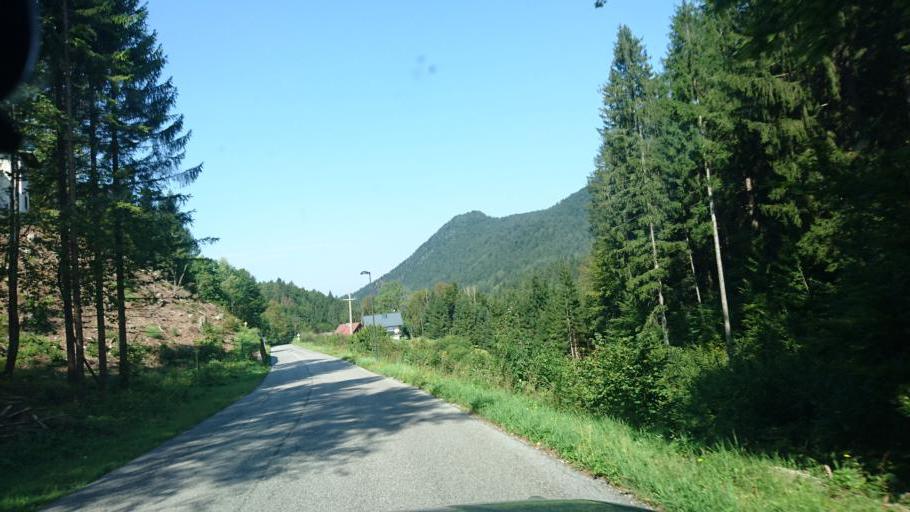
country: AT
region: Carinthia
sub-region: Politischer Bezirk Villach Land
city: Hohenthurn
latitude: 46.4941
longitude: 13.6669
